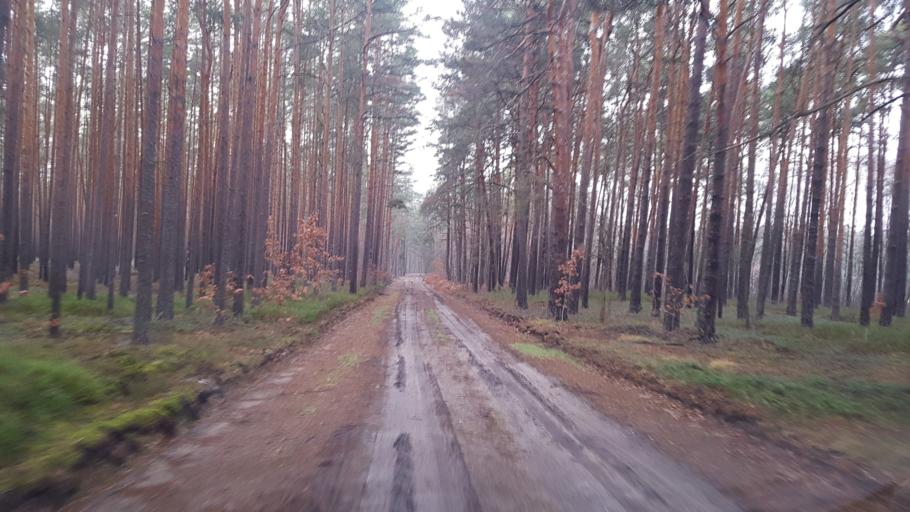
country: DE
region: Brandenburg
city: Ruckersdorf
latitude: 51.5819
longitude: 13.6076
